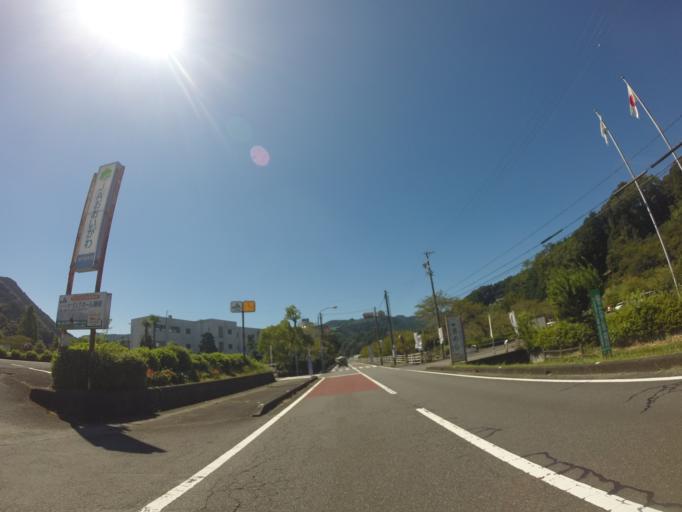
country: JP
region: Shizuoka
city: Fujieda
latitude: 34.9141
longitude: 138.2017
